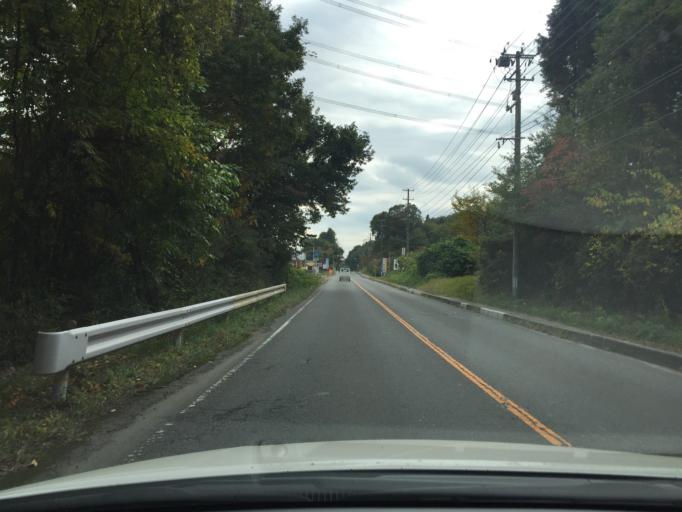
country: JP
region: Fukushima
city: Ishikawa
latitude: 37.0522
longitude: 140.3740
